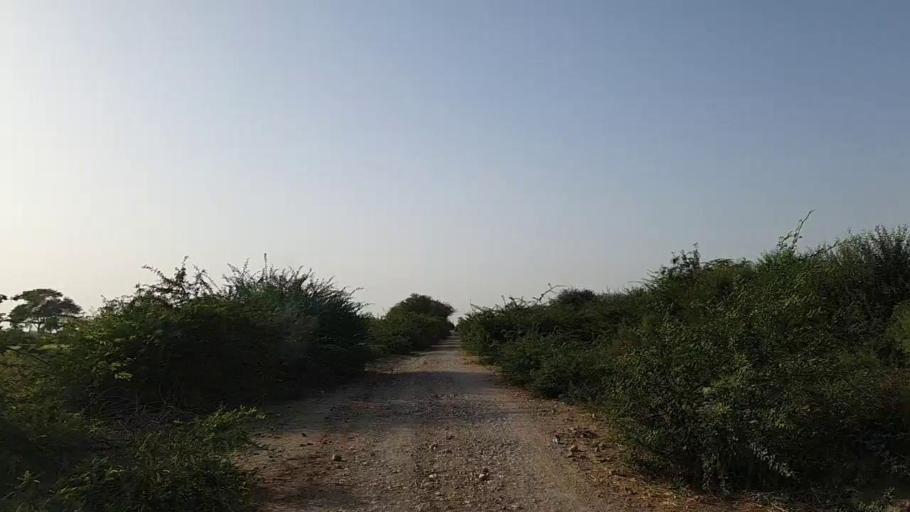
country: PK
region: Sindh
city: Jati
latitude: 24.3404
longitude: 68.1486
